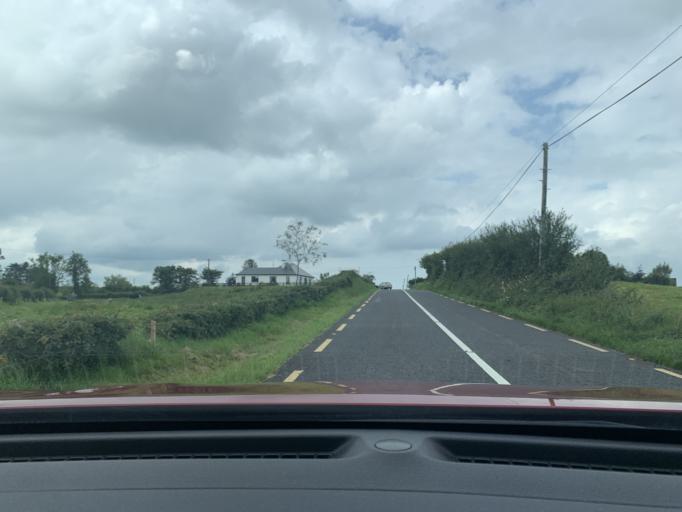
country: IE
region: Connaught
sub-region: Maigh Eo
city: Swinford
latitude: 53.8596
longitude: -8.8701
